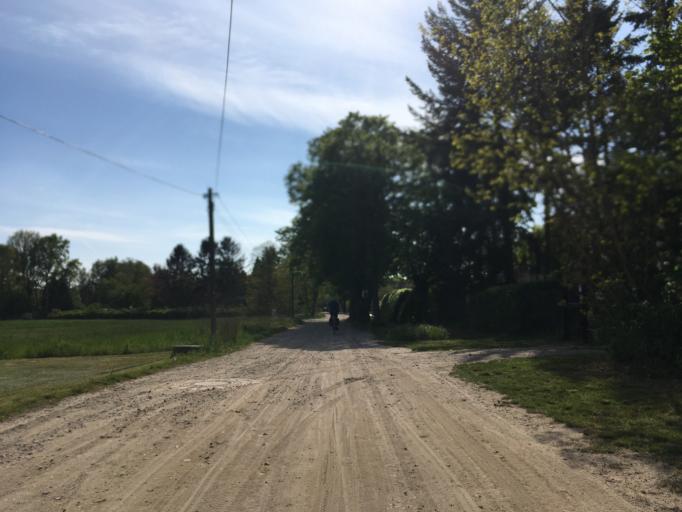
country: DE
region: Brandenburg
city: Bernau bei Berlin
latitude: 52.6663
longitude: 13.5460
